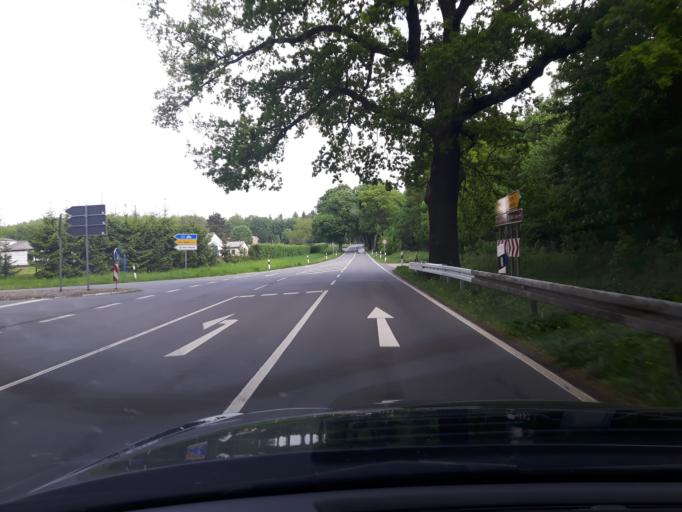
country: DE
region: Mecklenburg-Vorpommern
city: Gross Wokern
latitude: 53.6178
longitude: 12.4668
